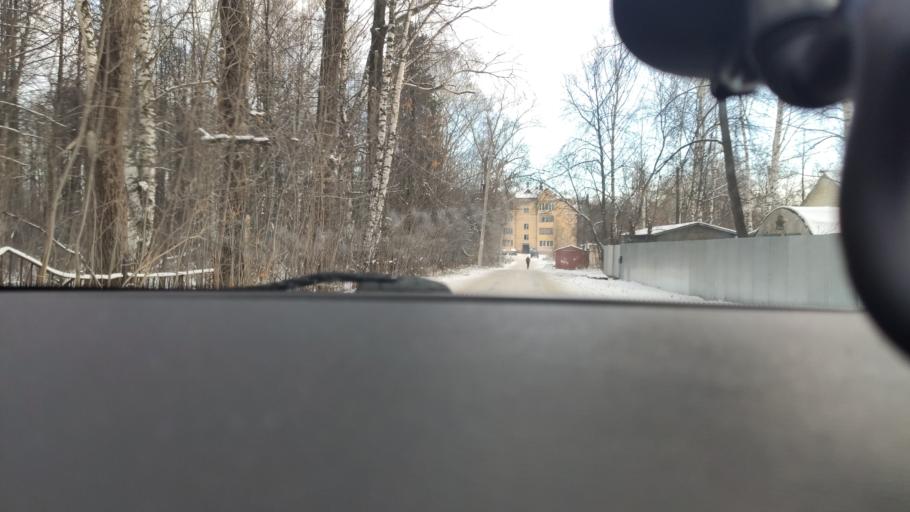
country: RU
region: Perm
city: Froly
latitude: 57.9487
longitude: 56.2706
